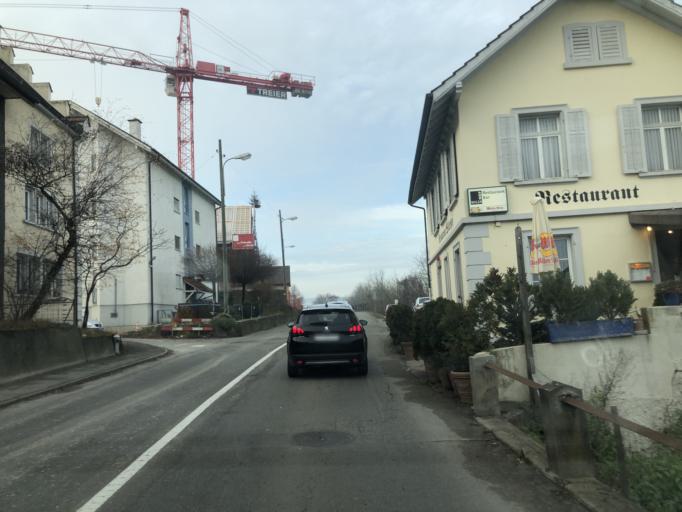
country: CH
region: Aargau
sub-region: Bezirk Baden
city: Turgi
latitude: 47.4866
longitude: 8.2650
